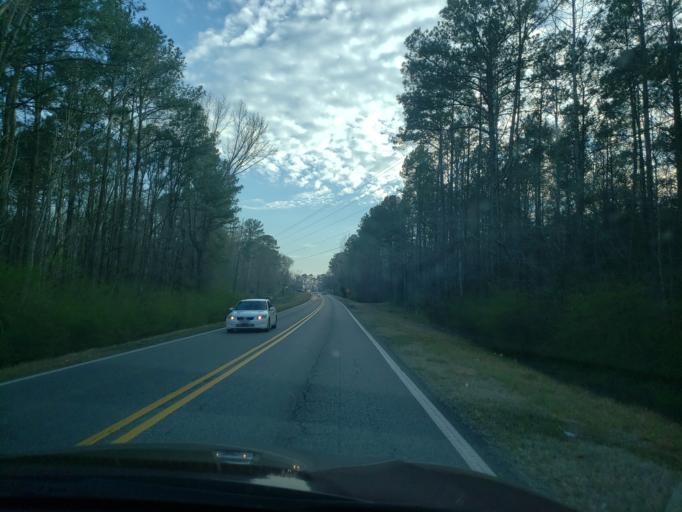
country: US
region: Alabama
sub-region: Hale County
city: Greensboro
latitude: 32.7204
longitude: -87.5931
